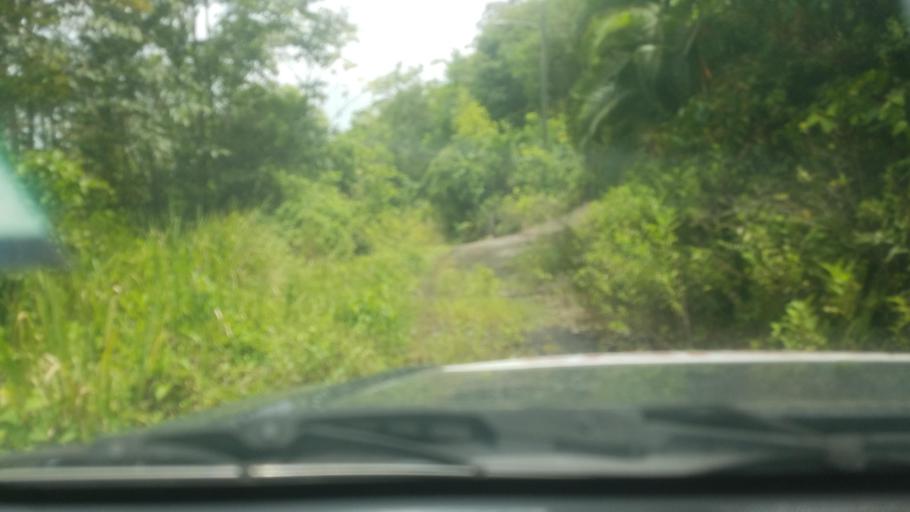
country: LC
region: Laborie Quarter
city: Laborie
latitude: 13.7589
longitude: -60.9979
